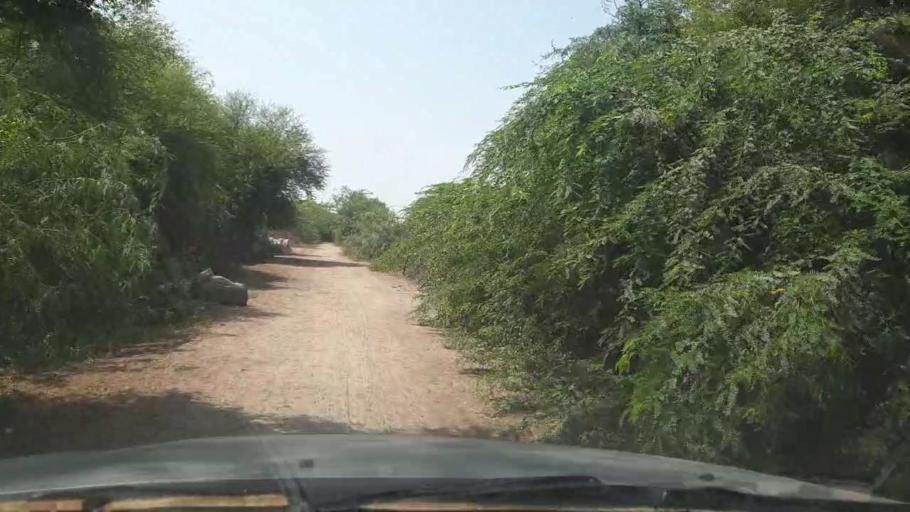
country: PK
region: Sindh
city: Chambar
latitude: 25.2064
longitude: 68.7811
